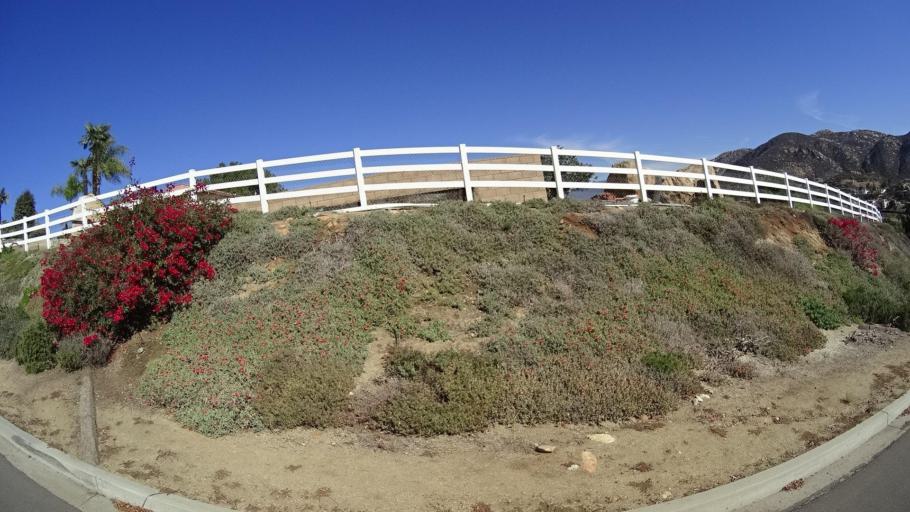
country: US
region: California
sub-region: San Diego County
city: Crest
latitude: 32.8561
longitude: -116.8699
